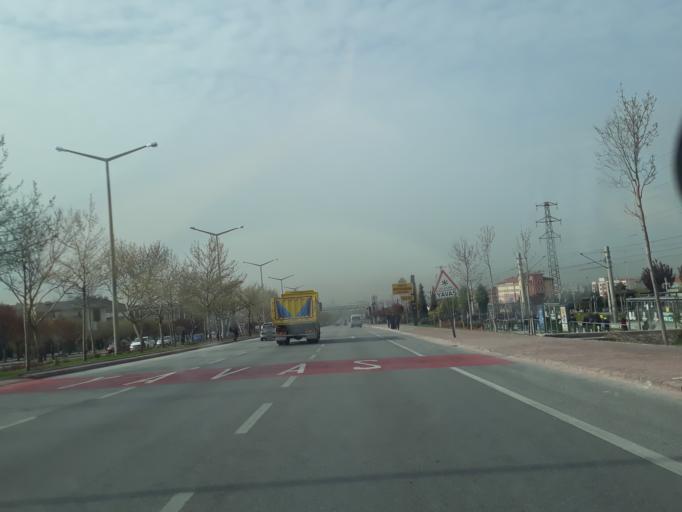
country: TR
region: Konya
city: Asagipinarbasi
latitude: 37.9897
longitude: 32.5181
